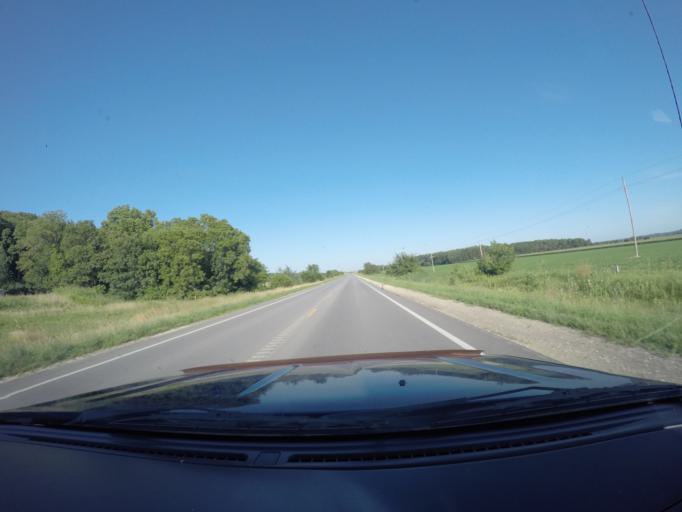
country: US
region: Kansas
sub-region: Douglas County
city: Lawrence
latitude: 39.0682
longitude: -95.3440
